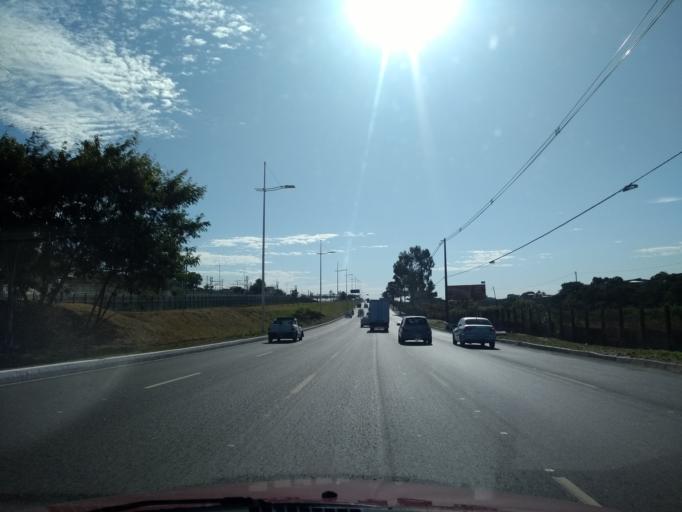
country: BR
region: Bahia
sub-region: Lauro De Freitas
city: Lauro de Freitas
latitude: -12.9236
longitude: -38.3719
